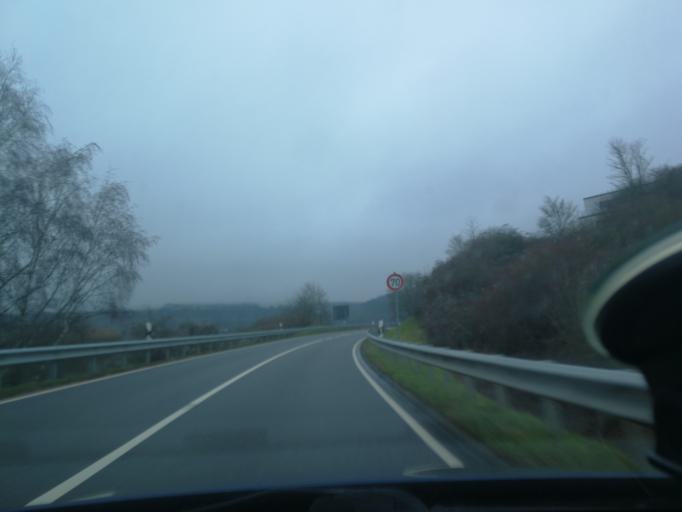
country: DE
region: Rheinland-Pfalz
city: Oberbillig
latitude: 49.7206
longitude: 6.5009
